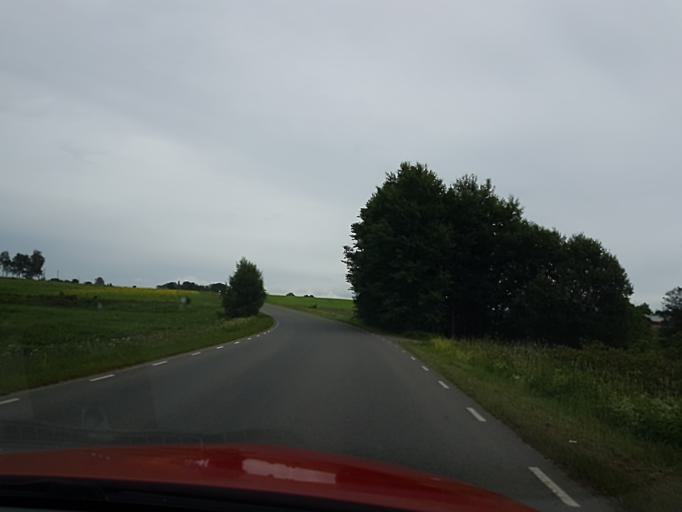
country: SE
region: Vaestra Goetaland
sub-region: Skovde Kommun
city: Skoevde
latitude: 58.3875
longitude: 13.8943
